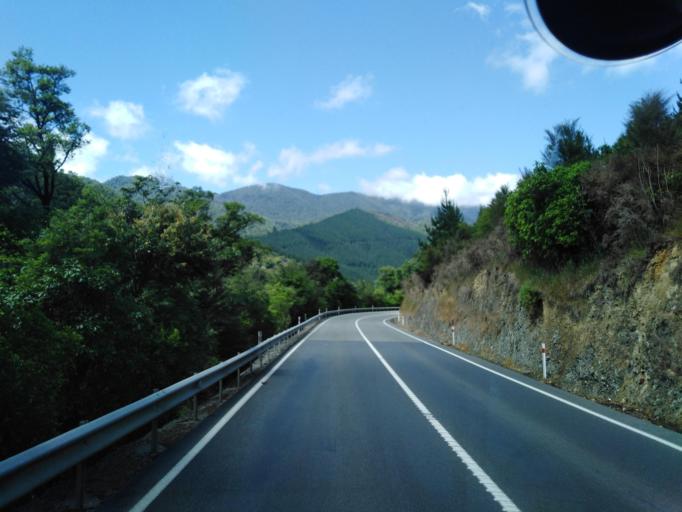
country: NZ
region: Nelson
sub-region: Nelson City
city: Nelson
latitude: -41.2252
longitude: 173.4362
